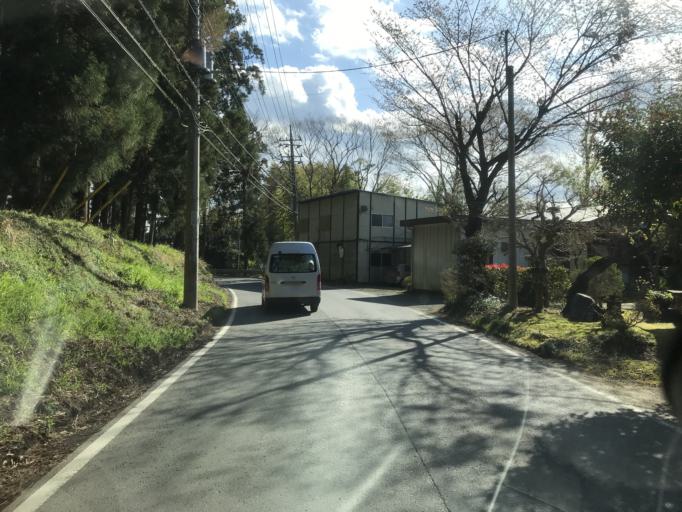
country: JP
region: Chiba
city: Sawara
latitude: 35.8395
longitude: 140.4289
